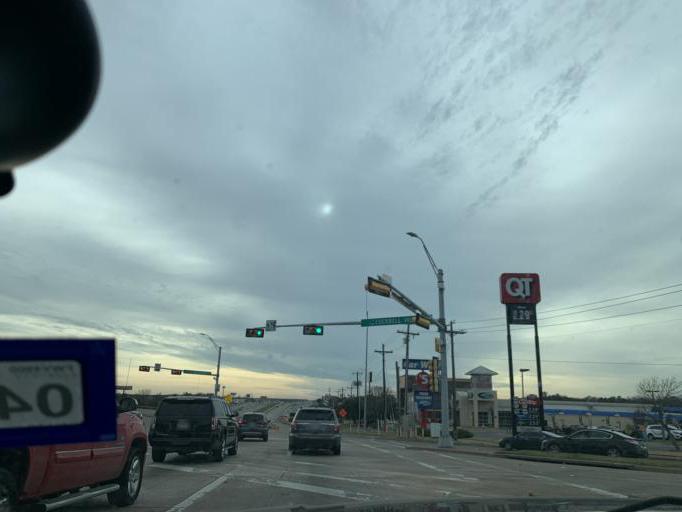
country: US
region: Texas
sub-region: Dallas County
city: Duncanville
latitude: 32.6421
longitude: -96.8912
